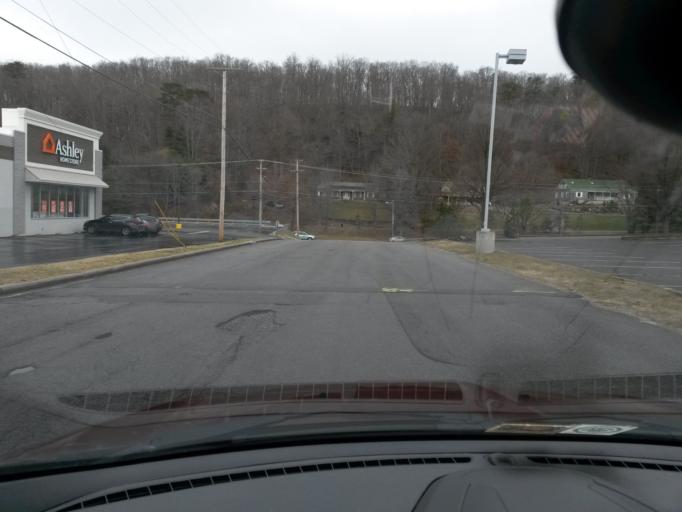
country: US
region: Virginia
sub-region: Tazewell County
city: Bluefield
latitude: 37.2400
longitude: -81.2526
